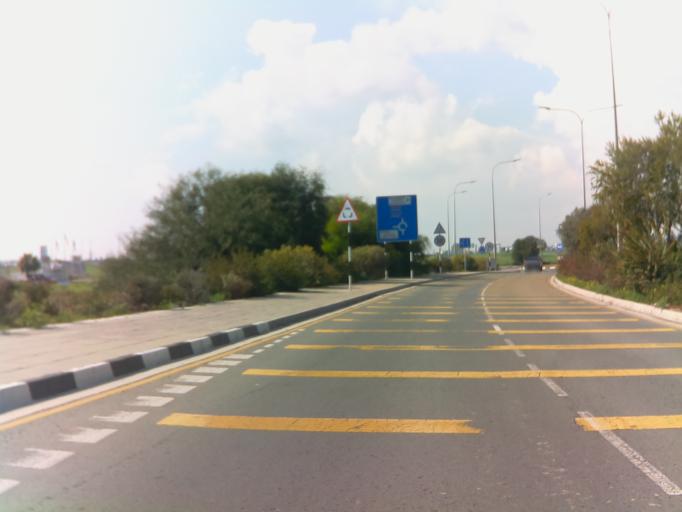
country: CY
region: Larnaka
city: Meneou
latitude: 34.8775
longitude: 33.6148
